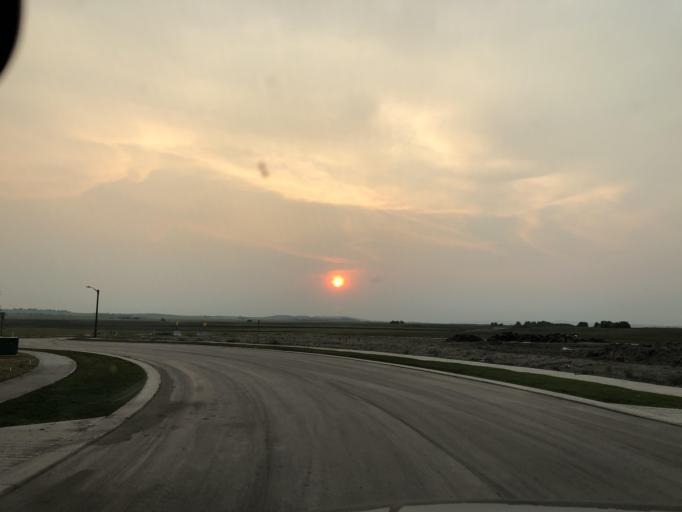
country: CA
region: Alberta
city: Cochrane
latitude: 51.1219
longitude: -114.3918
